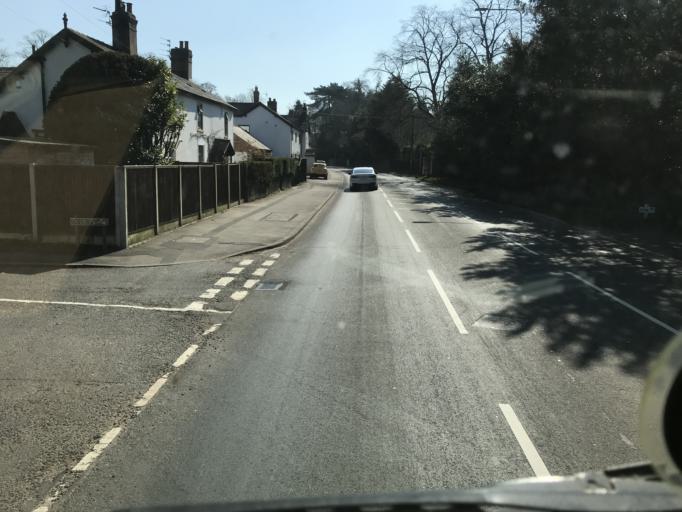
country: GB
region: England
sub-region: Cheshire East
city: Knutsford
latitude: 53.2973
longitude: -2.3608
